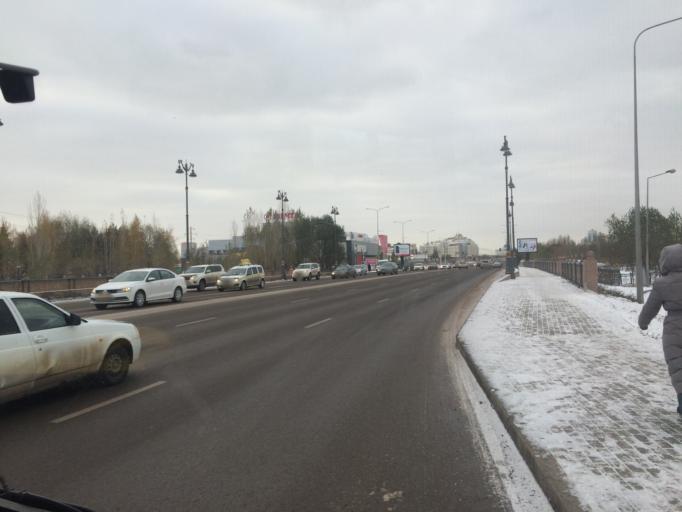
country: KZ
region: Astana Qalasy
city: Astana
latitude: 51.1508
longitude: 71.4444
